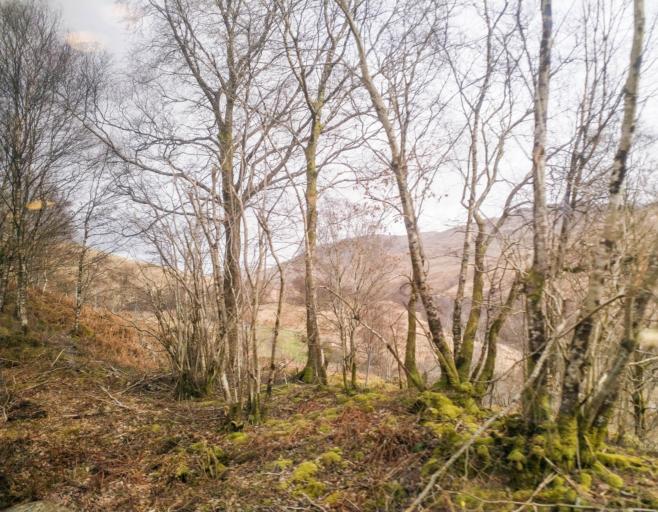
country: GB
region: Scotland
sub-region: Argyll and Bute
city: Garelochhead
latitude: 56.3503
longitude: -4.7028
